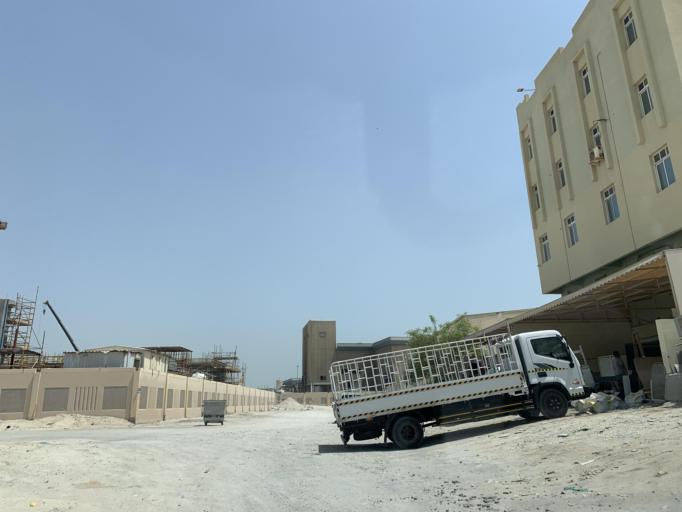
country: BH
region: Northern
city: Madinat `Isa
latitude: 26.1932
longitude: 50.5491
